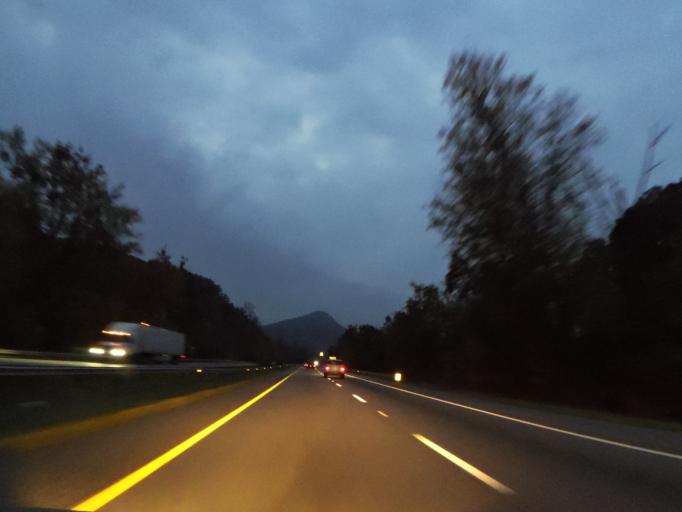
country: US
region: North Carolina
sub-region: Buncombe County
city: Black Mountain
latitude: 35.6266
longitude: -82.1748
